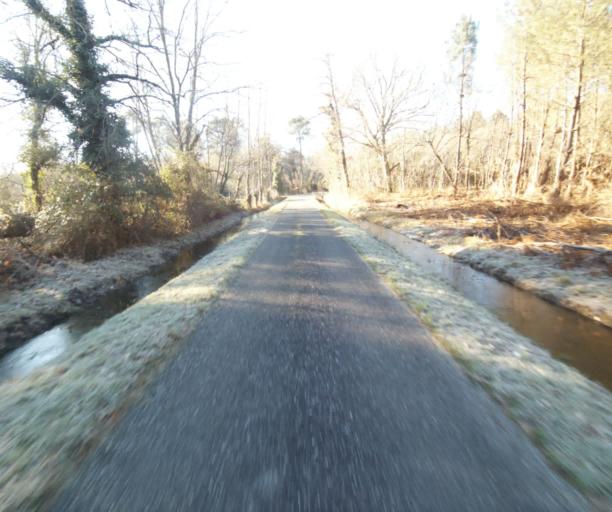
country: FR
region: Aquitaine
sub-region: Departement des Landes
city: Gabarret
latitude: 44.1144
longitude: 0.0612
